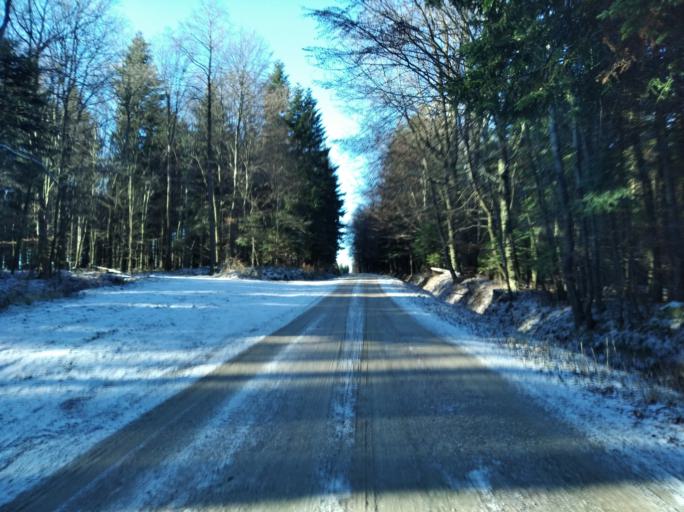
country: PL
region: Subcarpathian Voivodeship
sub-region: Powiat strzyzowski
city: Czudec
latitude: 49.9721
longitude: 21.8013
